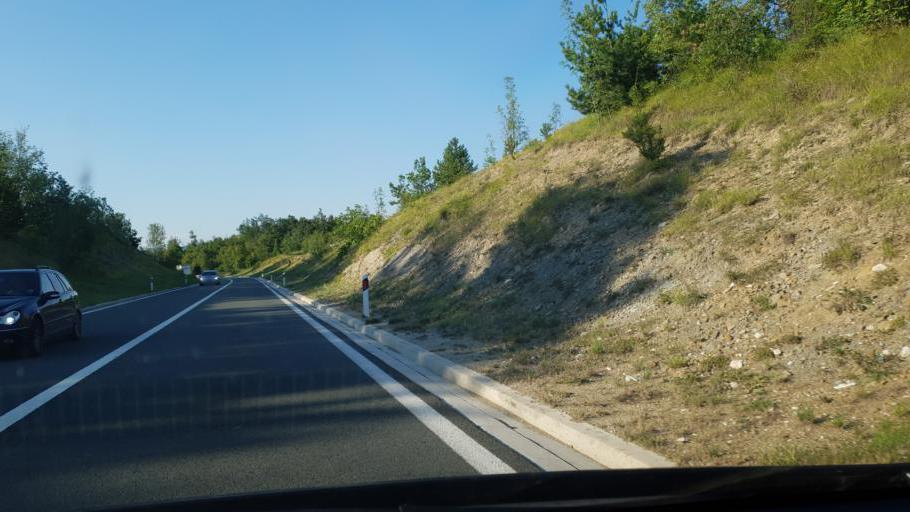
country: HR
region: Istarska
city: Buzet
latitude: 45.3234
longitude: 14.0754
